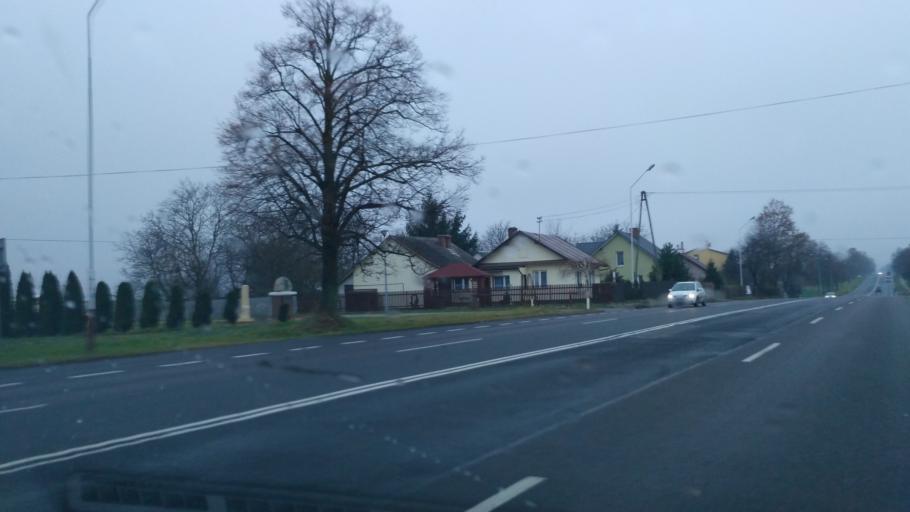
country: PL
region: Subcarpathian Voivodeship
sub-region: Powiat przeworski
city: Grzeska
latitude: 50.0619
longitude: 22.4643
